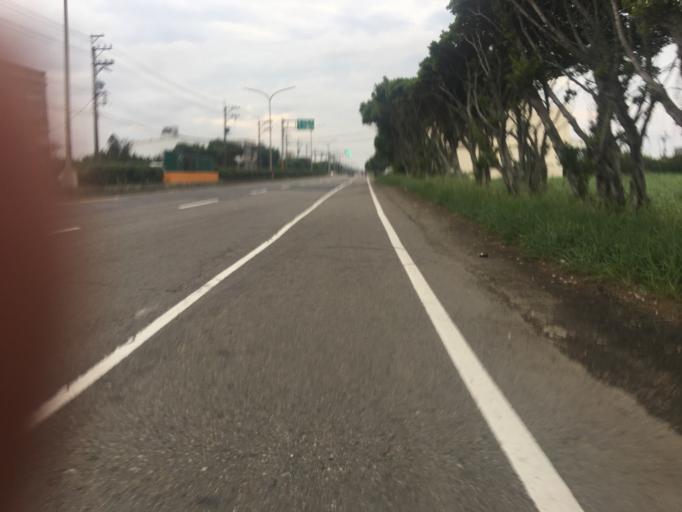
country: TW
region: Taiwan
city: Taoyuan City
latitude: 25.0894
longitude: 121.2282
